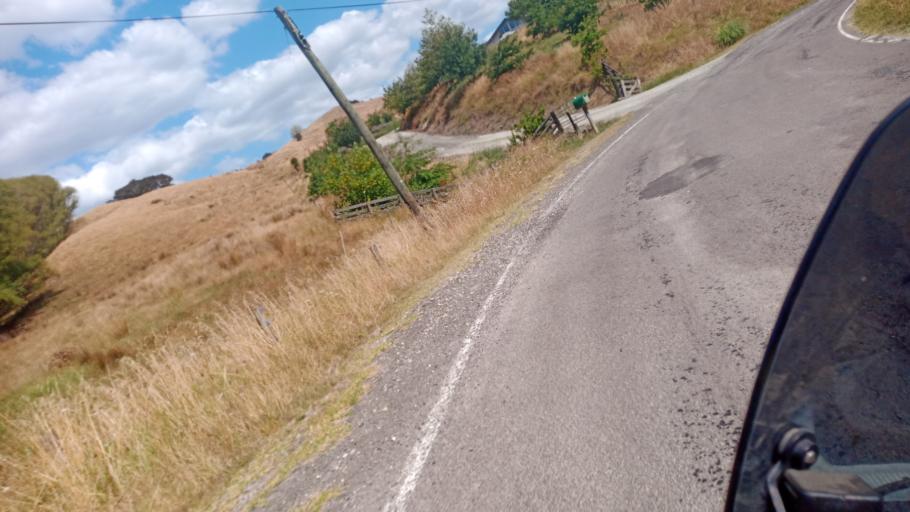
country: NZ
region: Gisborne
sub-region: Gisborne District
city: Gisborne
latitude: -38.5949
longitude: 177.7777
